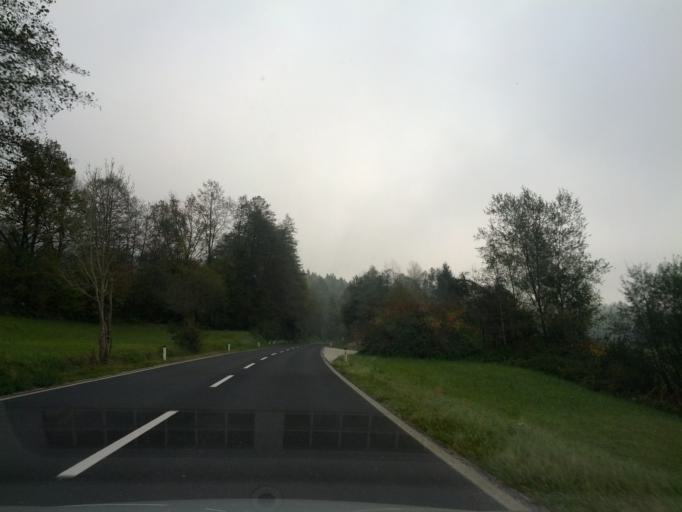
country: SI
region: Moravce
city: Moravce
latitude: 46.0927
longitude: 14.7469
